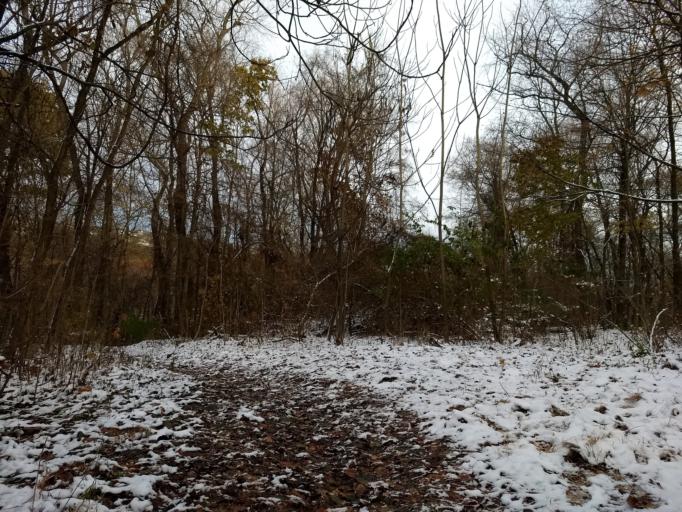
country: US
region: Pennsylvania
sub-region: Allegheny County
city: Mount Oliver
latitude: 40.4037
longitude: -80.0063
